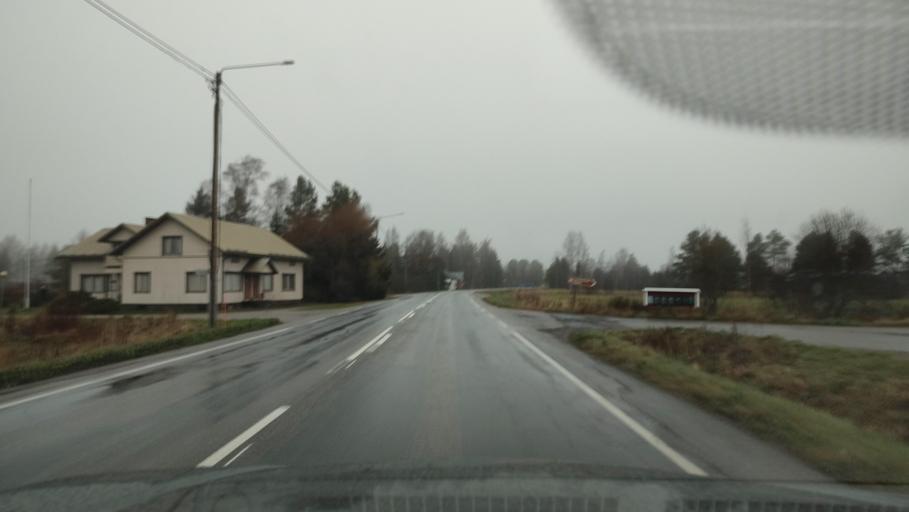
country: FI
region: Southern Ostrobothnia
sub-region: Suupohja
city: Karijoki
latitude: 62.1887
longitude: 21.7922
